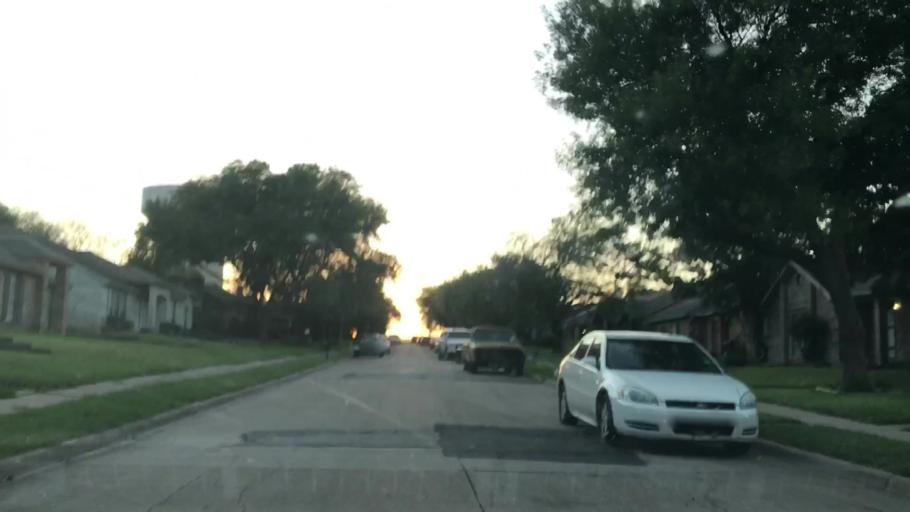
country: US
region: Texas
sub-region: Dallas County
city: Mesquite
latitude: 32.7609
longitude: -96.6286
